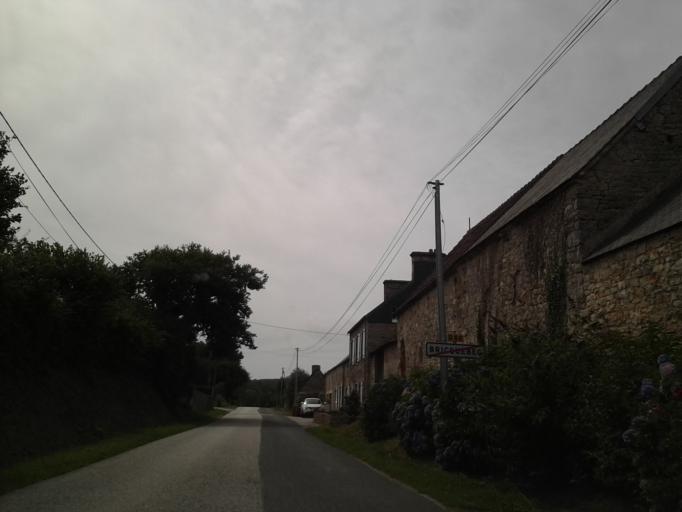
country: FR
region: Lower Normandy
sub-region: Departement de la Manche
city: Bricquebec
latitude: 49.4678
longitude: -1.6505
